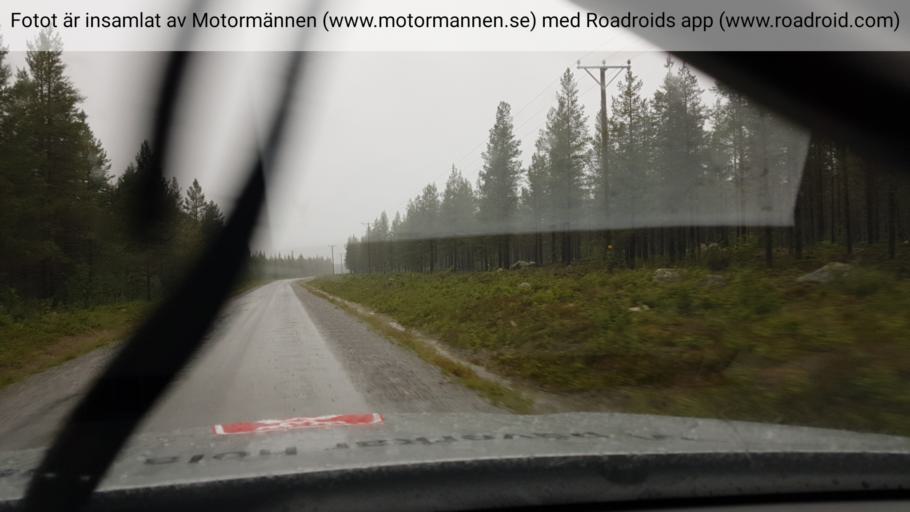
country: SE
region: Norrbotten
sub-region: Jokkmokks Kommun
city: Jokkmokk
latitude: 66.6142
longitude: 18.9508
